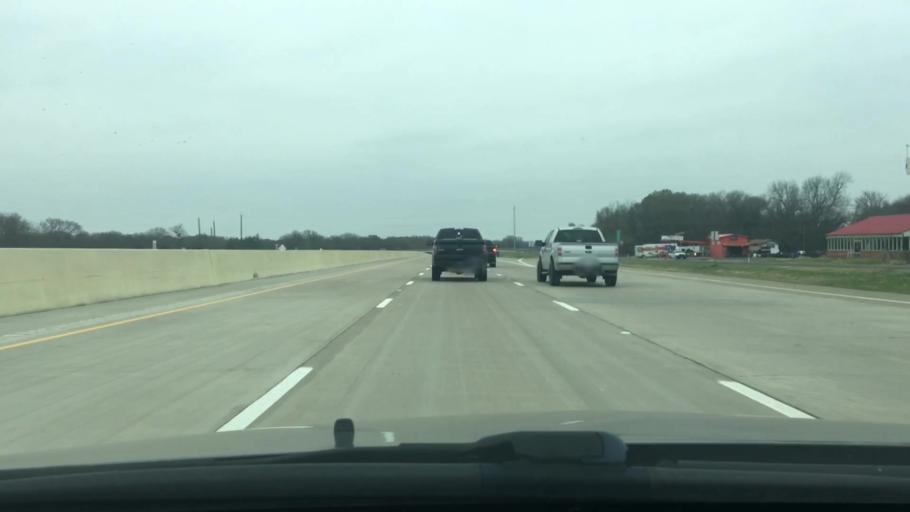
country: US
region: Texas
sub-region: Navarro County
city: Corsicana
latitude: 31.9674
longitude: -96.4215
